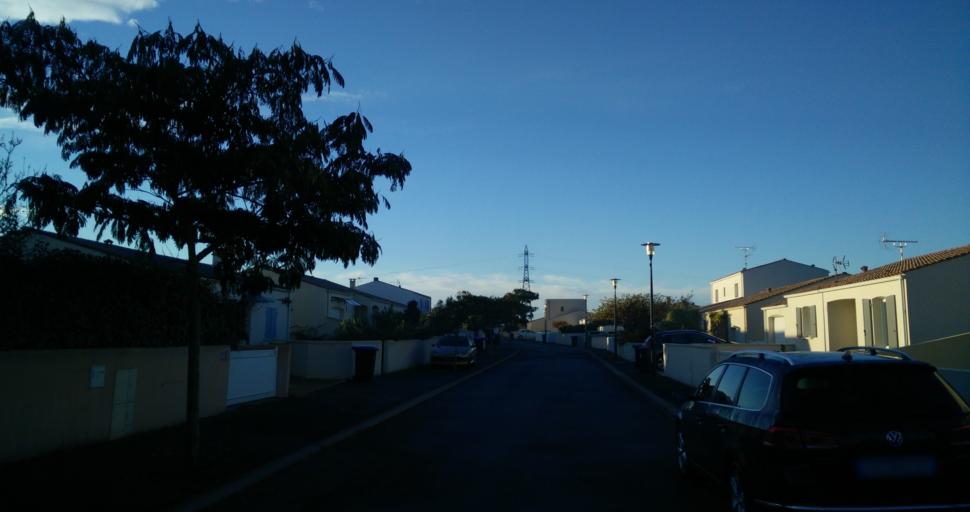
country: FR
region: Poitou-Charentes
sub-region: Departement de la Charente-Maritime
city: Puilboreau
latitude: 46.1851
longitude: -1.1262
